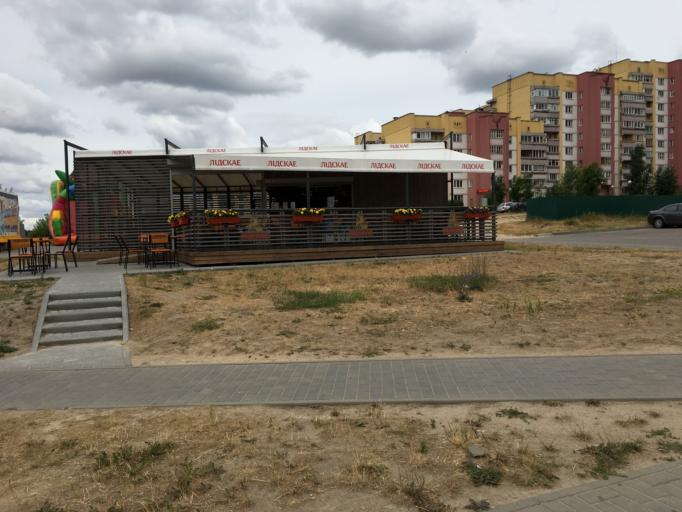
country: BY
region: Grodnenskaya
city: Hrodna
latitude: 53.7093
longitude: 23.8493
